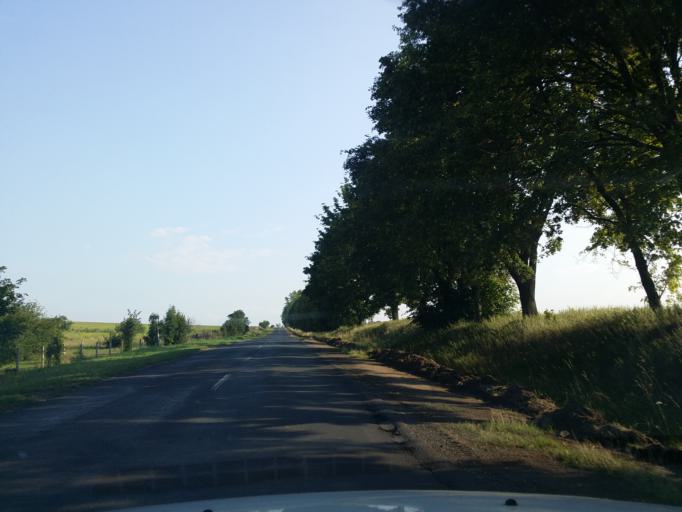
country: HU
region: Borsod-Abauj-Zemplen
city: Abaujszanto
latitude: 48.3726
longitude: 21.2155
